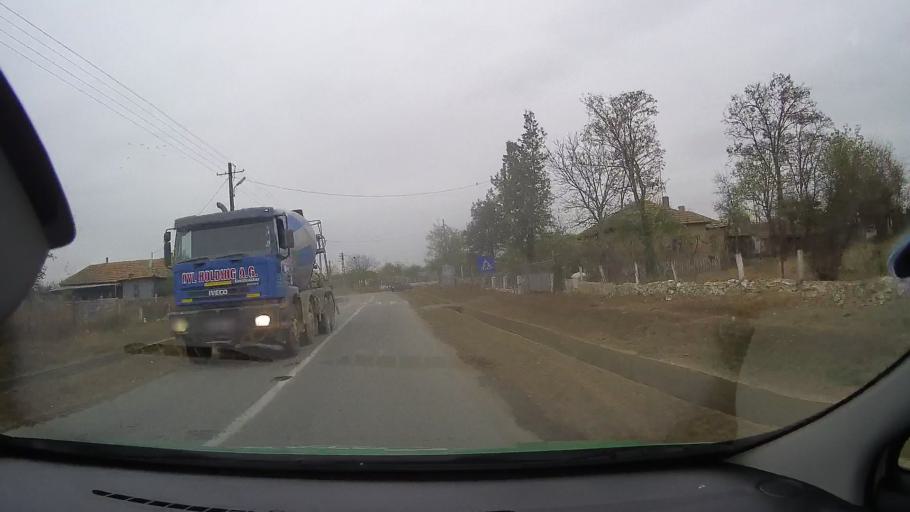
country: RO
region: Constanta
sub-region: Comuna Pantelimon
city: Pantelimon
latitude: 44.5987
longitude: 28.3302
